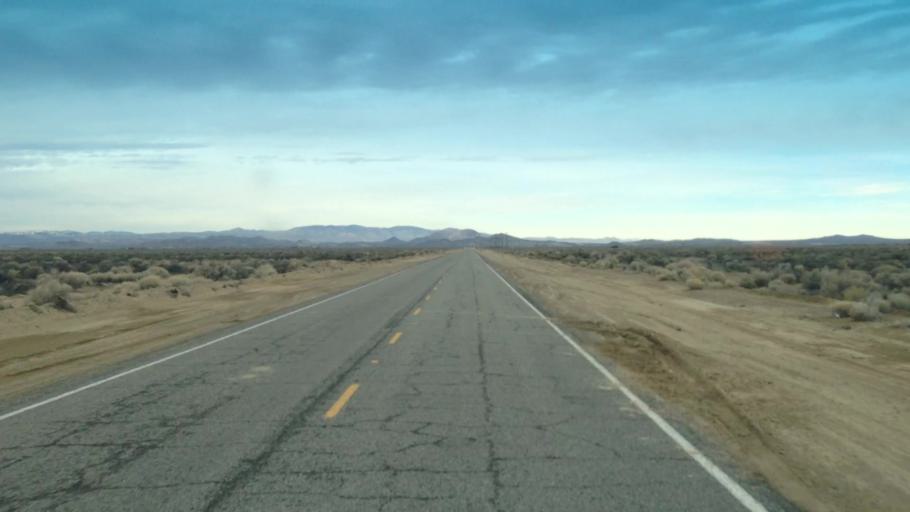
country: US
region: California
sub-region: Los Angeles County
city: Lancaster
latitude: 34.7504
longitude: -118.1843
